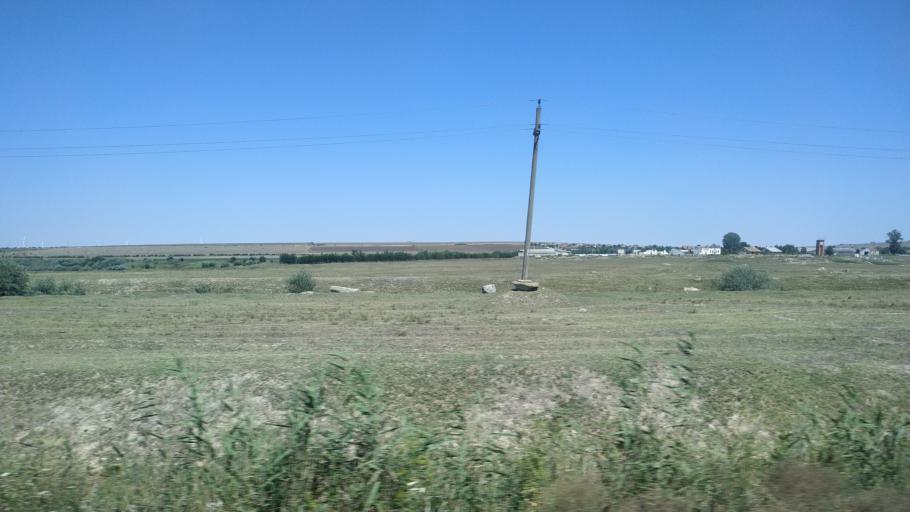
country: RO
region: Constanta
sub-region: Comuna Mircea Voda
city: Satu Nou
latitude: 44.2600
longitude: 28.2116
